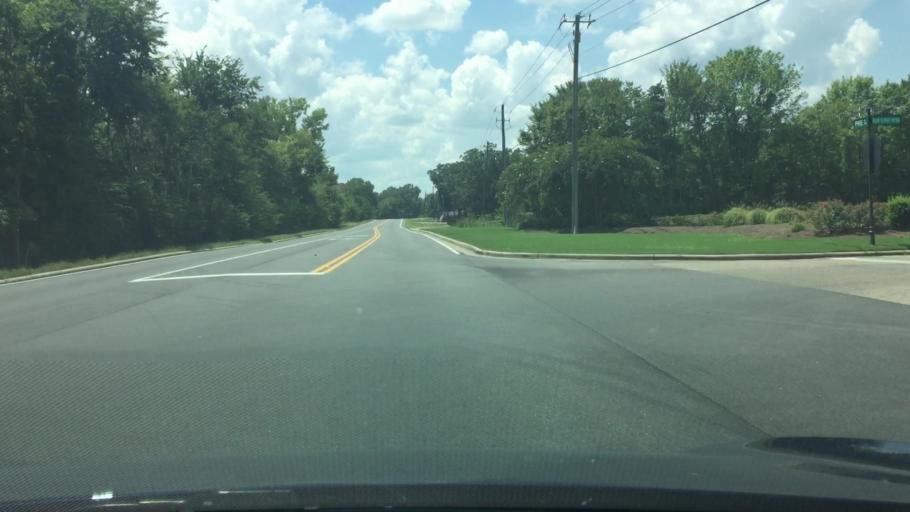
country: US
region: Alabama
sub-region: Montgomery County
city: Pike Road
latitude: 32.3241
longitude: -86.0945
